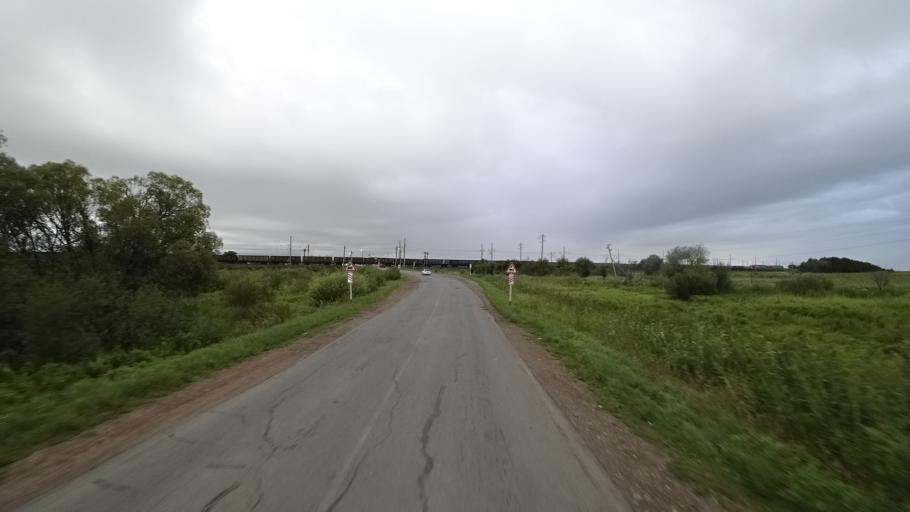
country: RU
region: Primorskiy
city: Chernigovka
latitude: 44.3629
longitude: 132.5526
